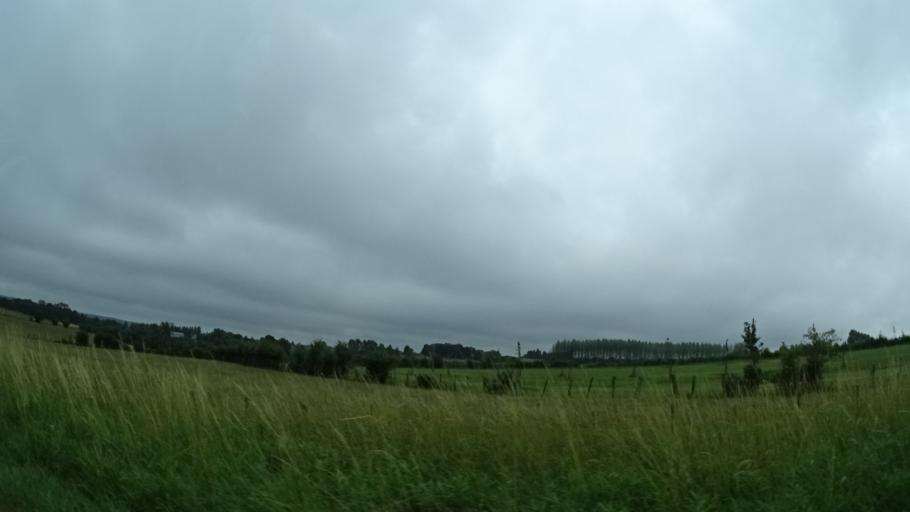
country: BE
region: Wallonia
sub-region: Province du Luxembourg
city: Habay-la-Vieille
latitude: 49.7173
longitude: 5.6831
